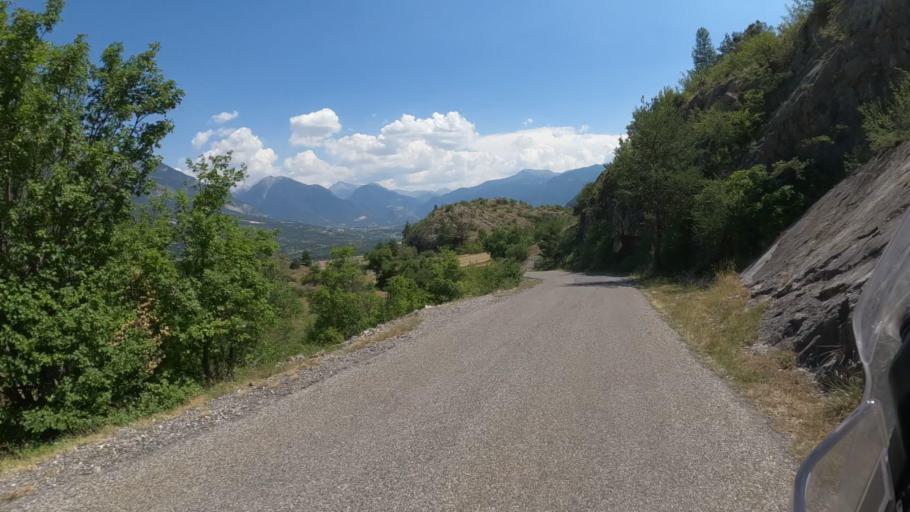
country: FR
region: Provence-Alpes-Cote d'Azur
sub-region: Departement des Hautes-Alpes
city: Guillestre
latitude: 44.7112
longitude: 6.5852
